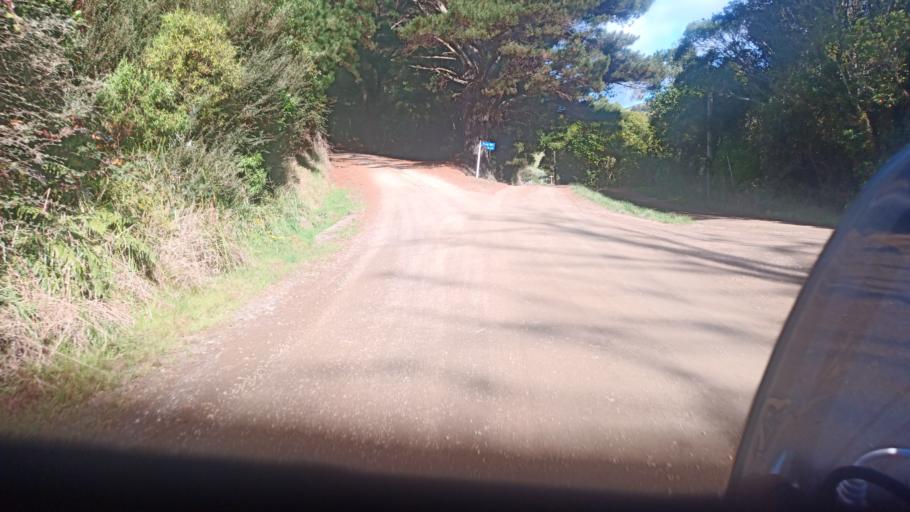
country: NZ
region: Bay of Plenty
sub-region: Opotiki District
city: Opotiki
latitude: -38.4417
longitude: 177.5360
